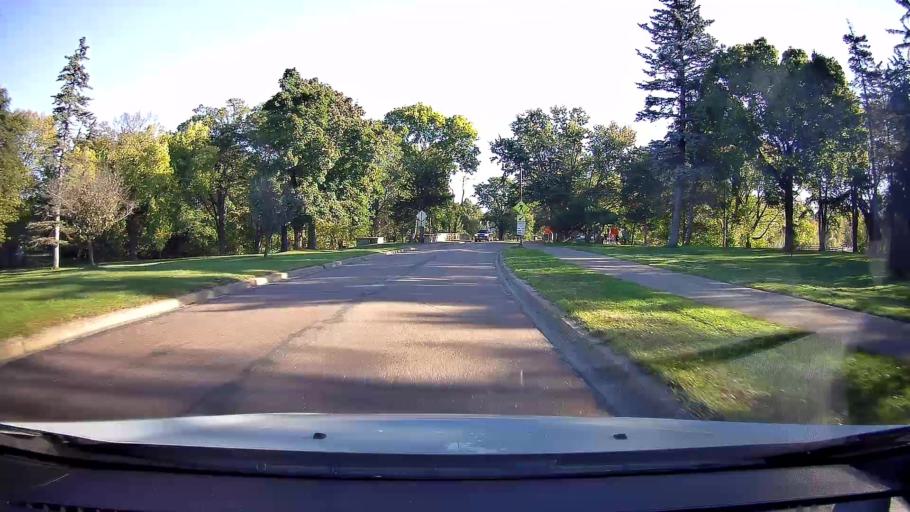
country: US
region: Minnesota
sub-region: Hennepin County
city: Richfield
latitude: 44.9147
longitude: -93.2426
